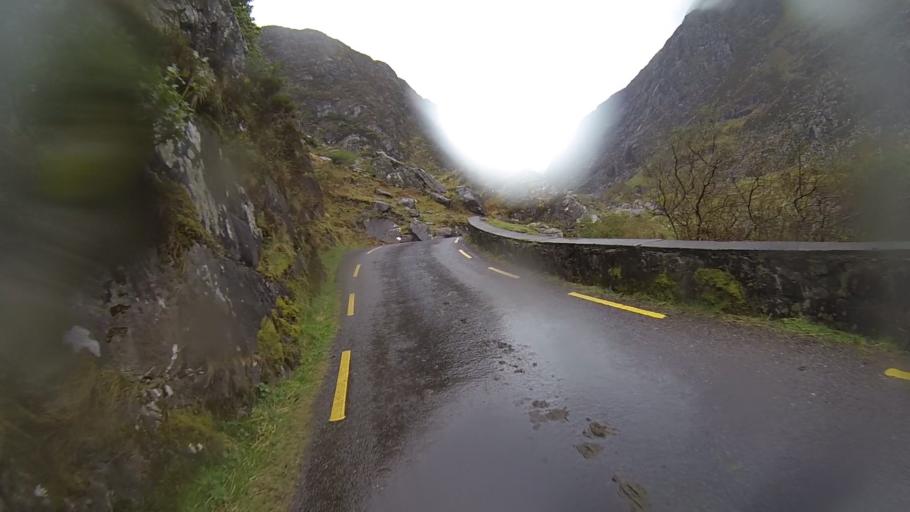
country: IE
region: Munster
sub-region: Ciarrai
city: Cill Airne
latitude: 52.0120
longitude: -9.6370
